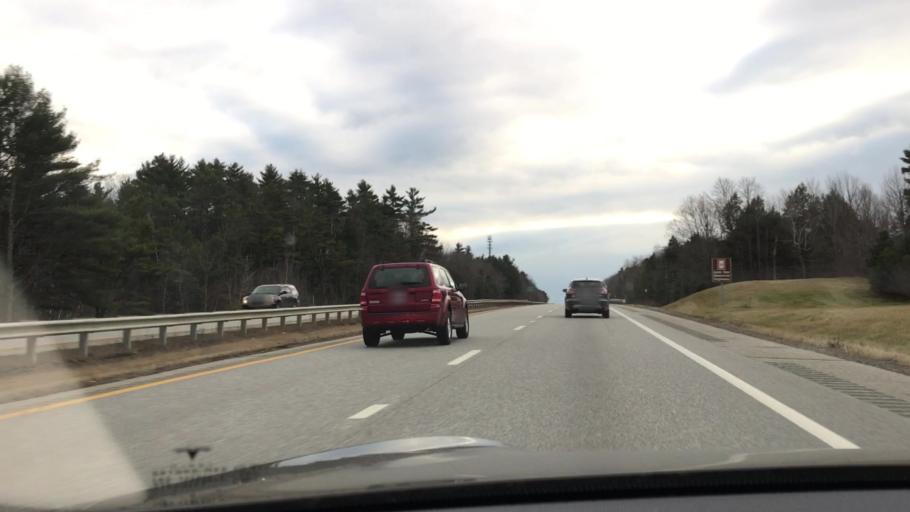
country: US
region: Maine
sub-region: Kennebec County
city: Hallowell
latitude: 44.2729
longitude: -69.8065
